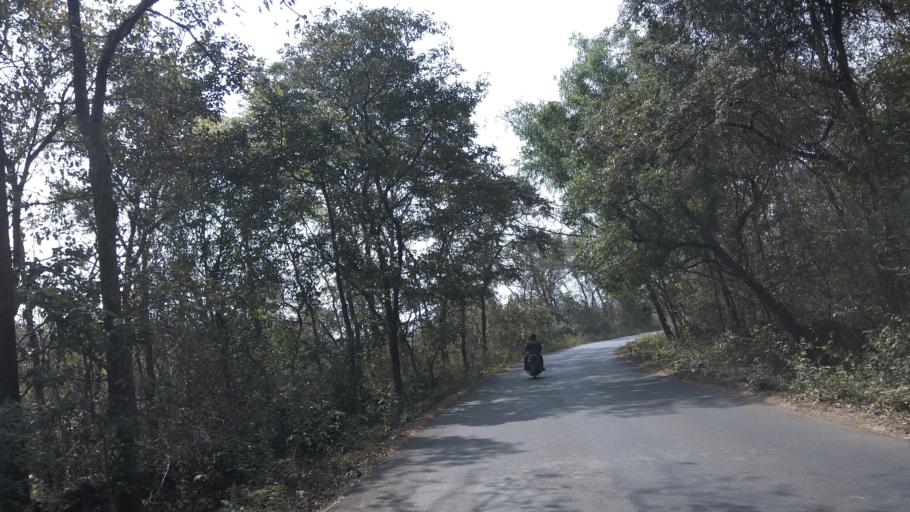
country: IN
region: Goa
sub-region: South Goa
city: Sanvordem
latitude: 15.3654
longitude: 74.2353
